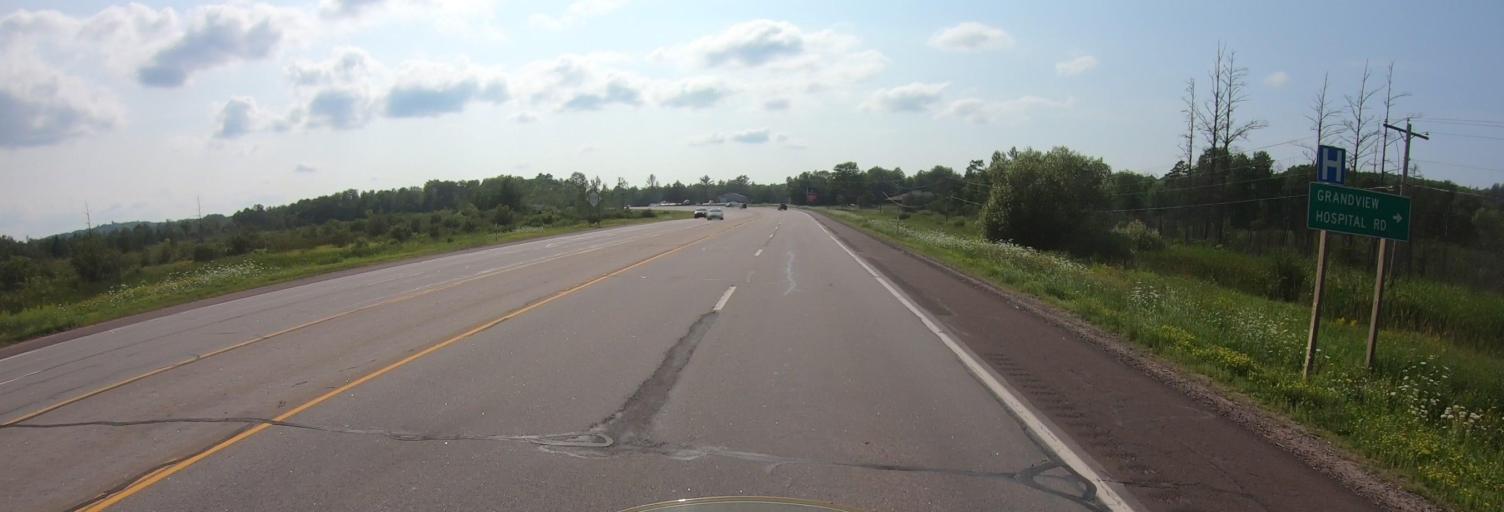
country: US
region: Michigan
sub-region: Gogebic County
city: Bessemer
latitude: 46.4778
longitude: -90.1015
